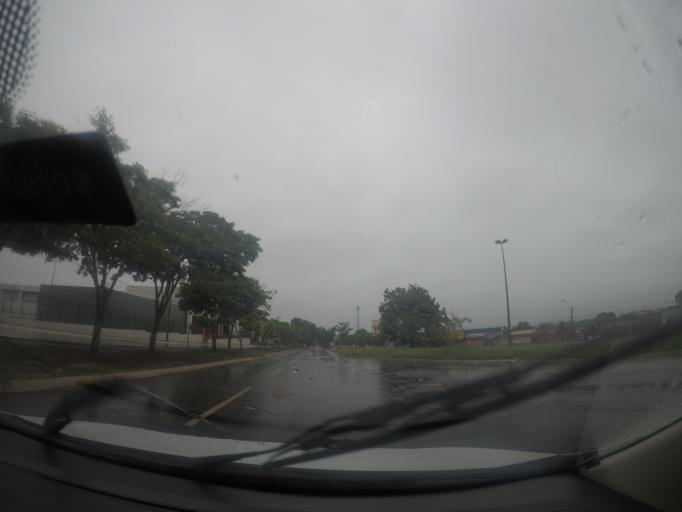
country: BR
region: Goias
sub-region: Goiania
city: Goiania
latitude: -16.5926
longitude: -49.3354
